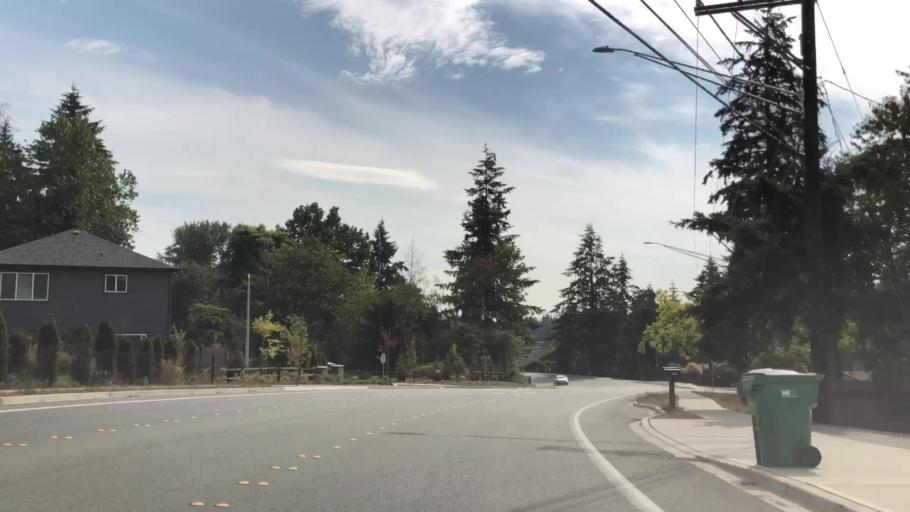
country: US
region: Washington
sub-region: Snohomish County
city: Martha Lake
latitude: 47.8386
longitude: -122.2358
